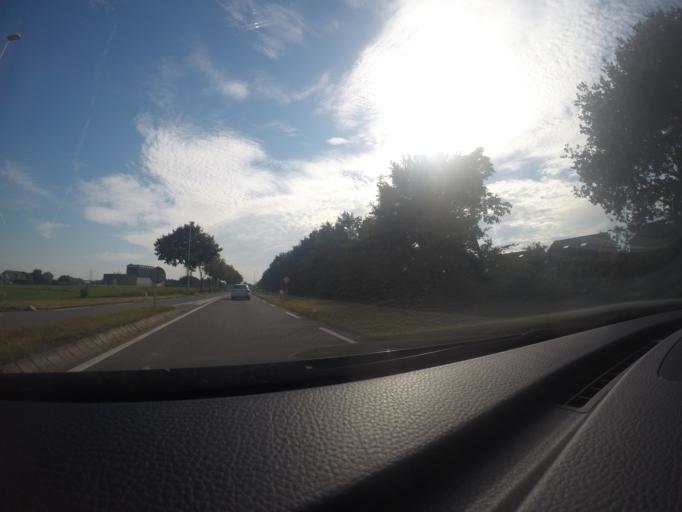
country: NL
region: Gelderland
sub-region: Gemeente Doetinchem
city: Doetinchem
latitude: 51.9651
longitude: 6.2184
